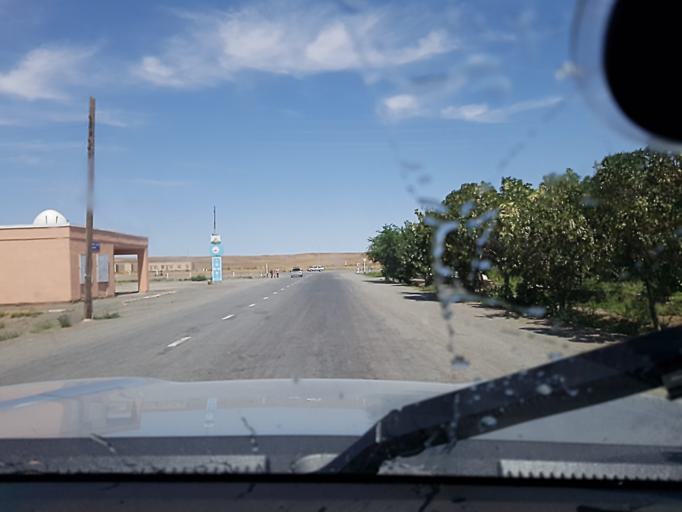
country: UZ
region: Karakalpakstan
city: Mang'it Shahri
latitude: 42.2439
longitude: 60.1514
